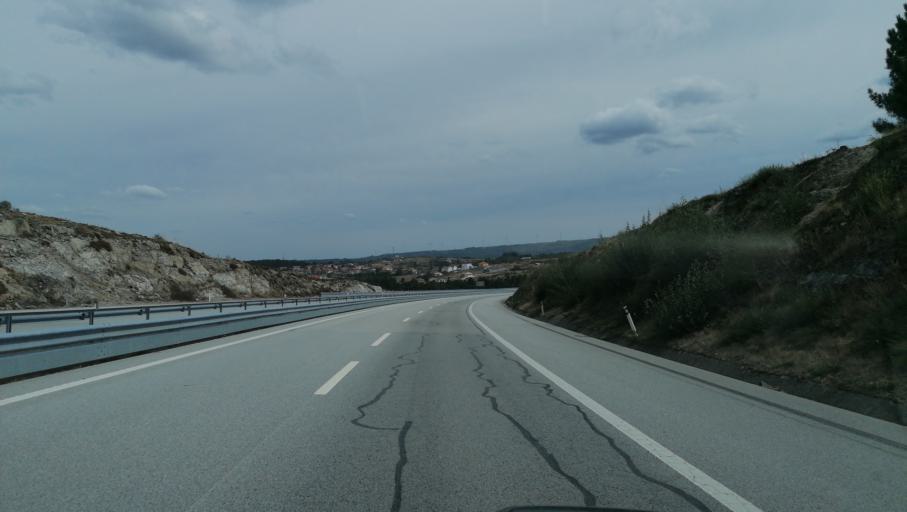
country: PT
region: Vila Real
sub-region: Vila Pouca de Aguiar
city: Vila Pouca de Aguiar
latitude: 41.5016
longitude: -7.7088
